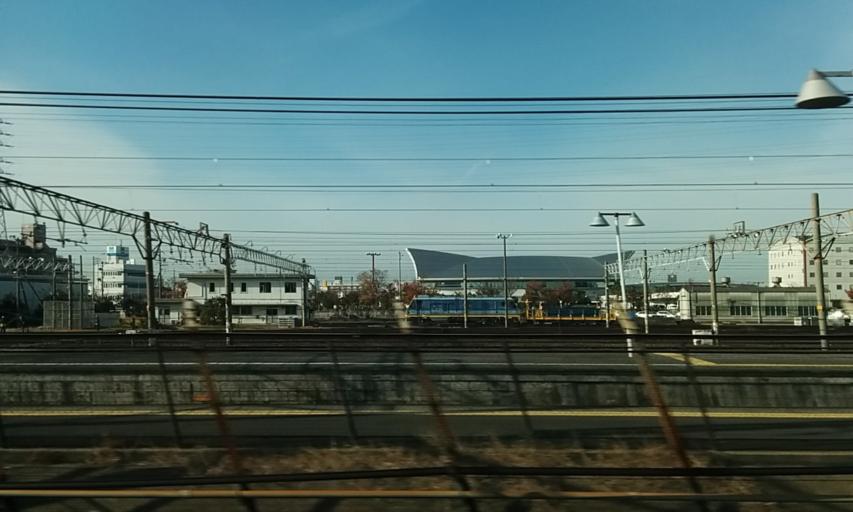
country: JP
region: Aichi
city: Nagoya-shi
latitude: 35.0945
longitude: 136.9271
